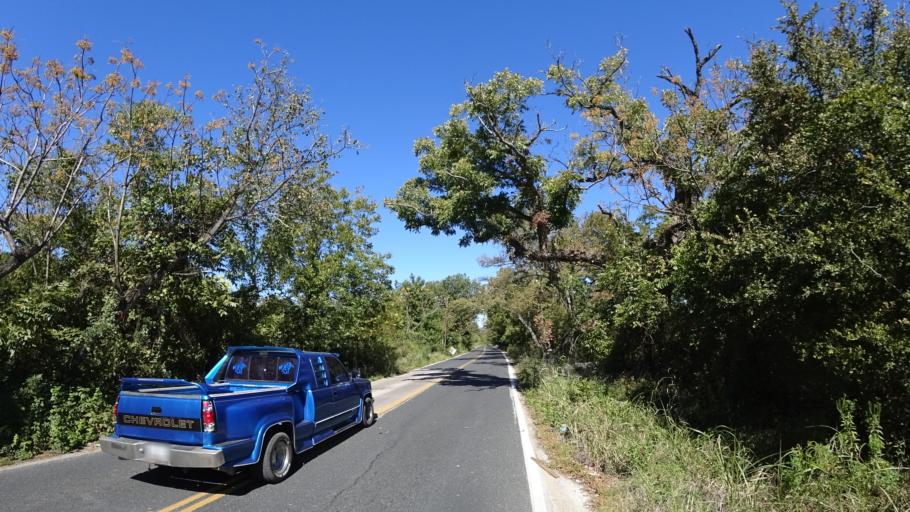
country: US
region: Texas
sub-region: Travis County
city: Hornsby Bend
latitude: 30.2869
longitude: -97.6538
